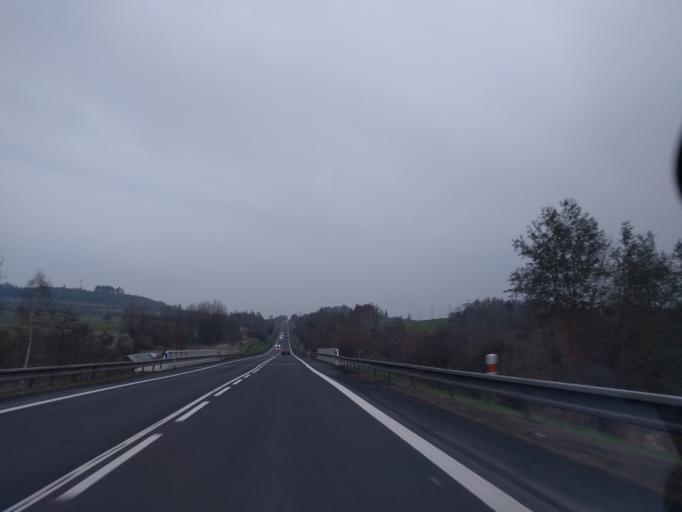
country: CZ
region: Karlovarsky
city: Zlutice
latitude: 50.1351
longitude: 13.1454
